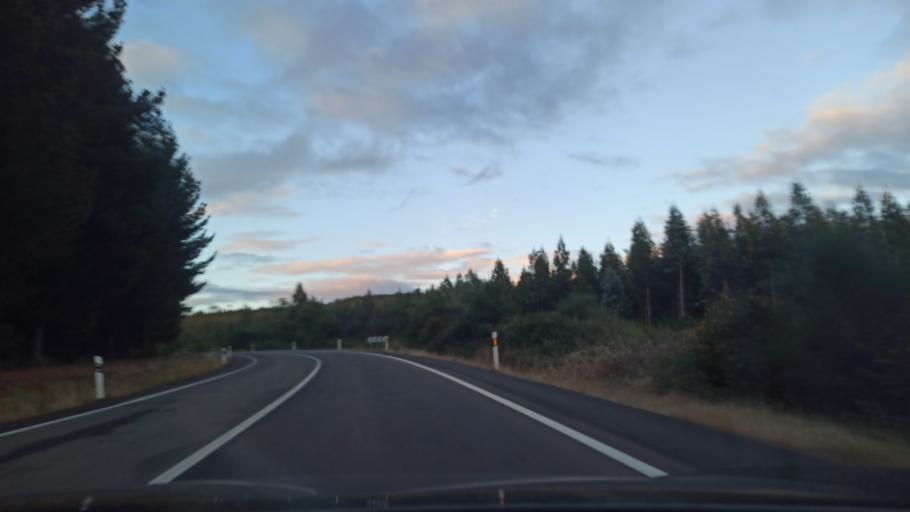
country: ES
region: Galicia
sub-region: Provincia de Lugo
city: Monterroso
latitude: 42.8018
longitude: -7.7875
